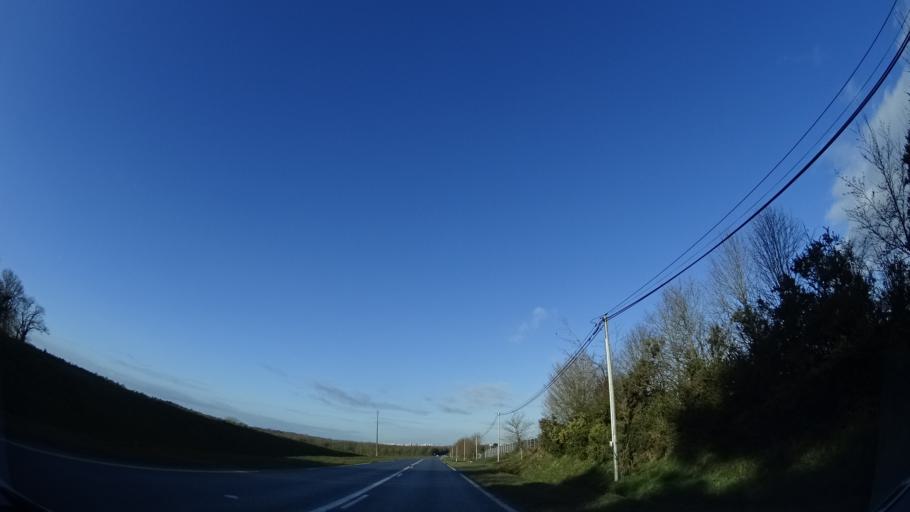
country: FR
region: Brittany
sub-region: Departement d'Ille-et-Vilaine
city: Vern-sur-Seiche
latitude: 48.0754
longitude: -1.5819
